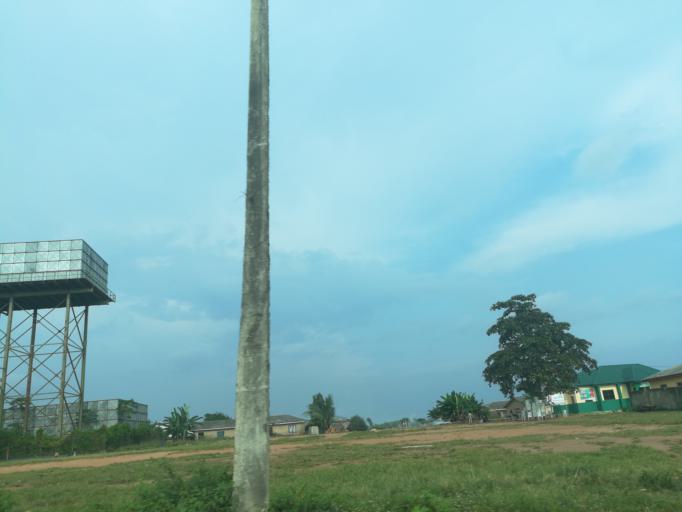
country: NG
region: Lagos
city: Ikorodu
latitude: 6.6604
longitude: 3.6696
